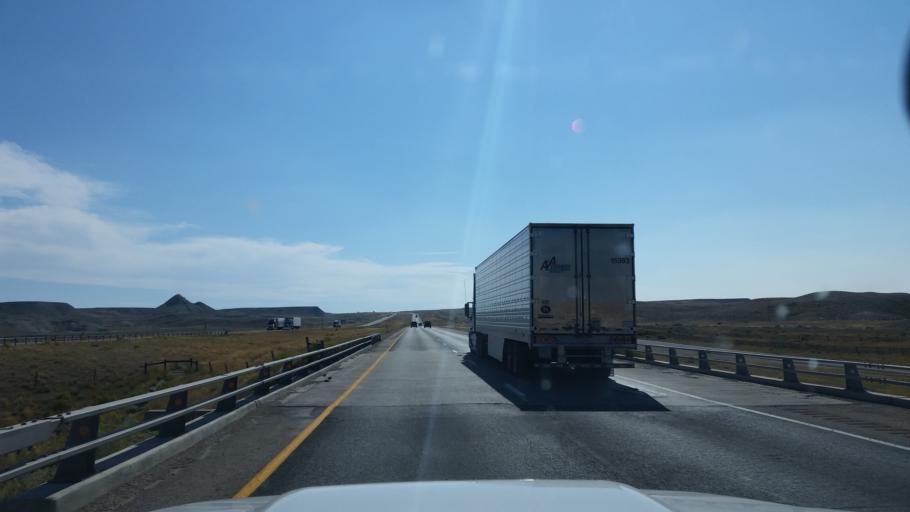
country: US
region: Wyoming
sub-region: Uinta County
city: Lyman
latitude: 41.5099
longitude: -109.9853
